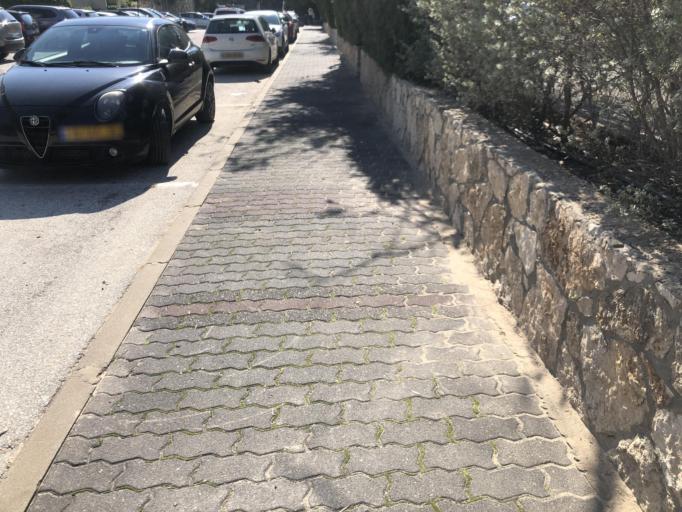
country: PS
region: West Bank
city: Az Zawiyah
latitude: 32.1105
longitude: 35.0353
